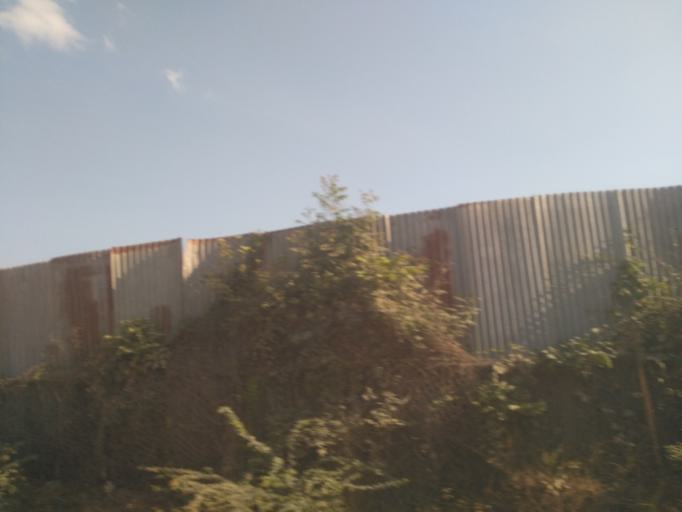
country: TZ
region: Pwani
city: Vikindu
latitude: -6.9191
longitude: 39.2641
